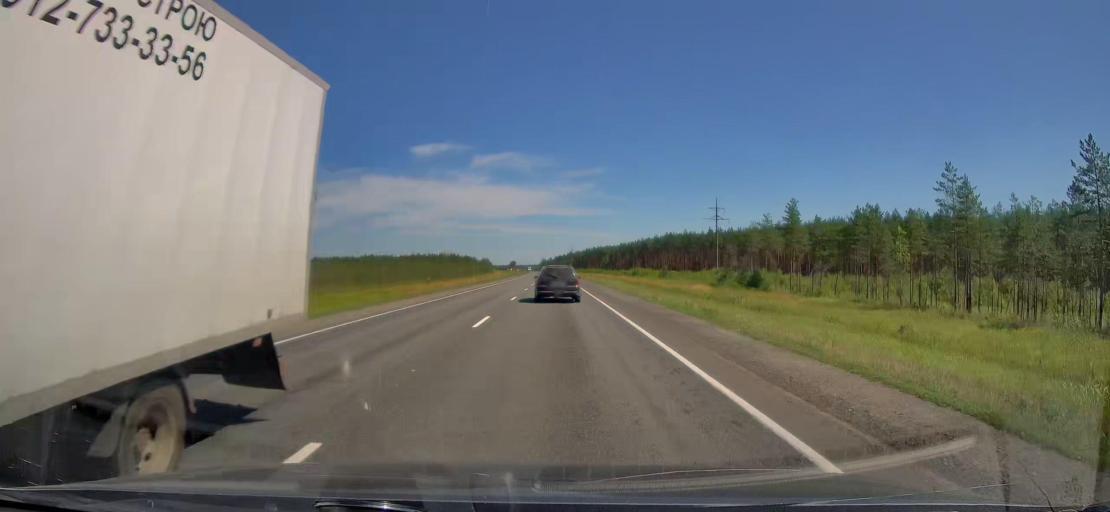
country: RU
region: Vologda
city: Khokhlovo
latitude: 58.9299
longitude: 37.2590
